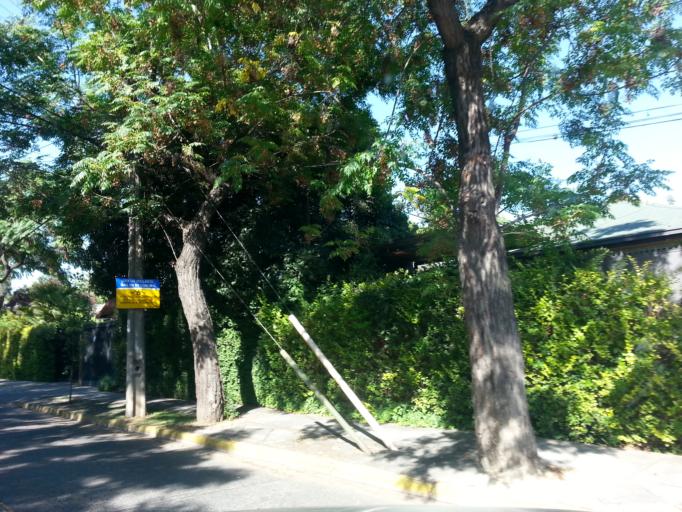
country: CL
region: Santiago Metropolitan
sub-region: Provincia de Santiago
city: Villa Presidente Frei, Nunoa, Santiago, Chile
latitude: -33.3924
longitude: -70.5870
